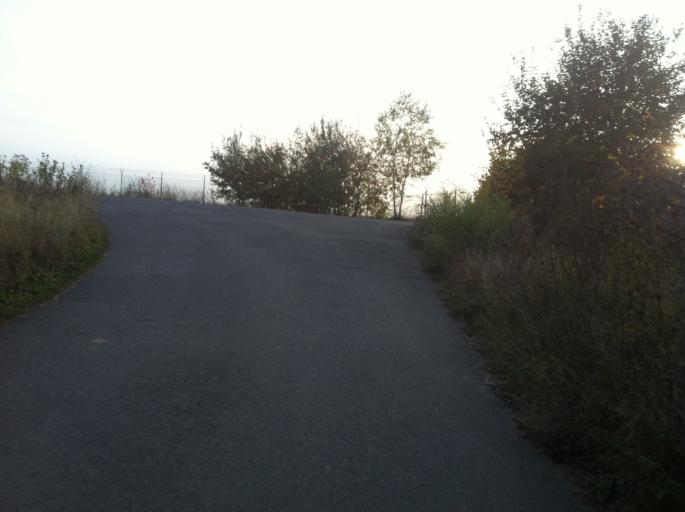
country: DE
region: Rheinland-Pfalz
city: Wackernheim
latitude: 49.9718
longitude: 8.1564
